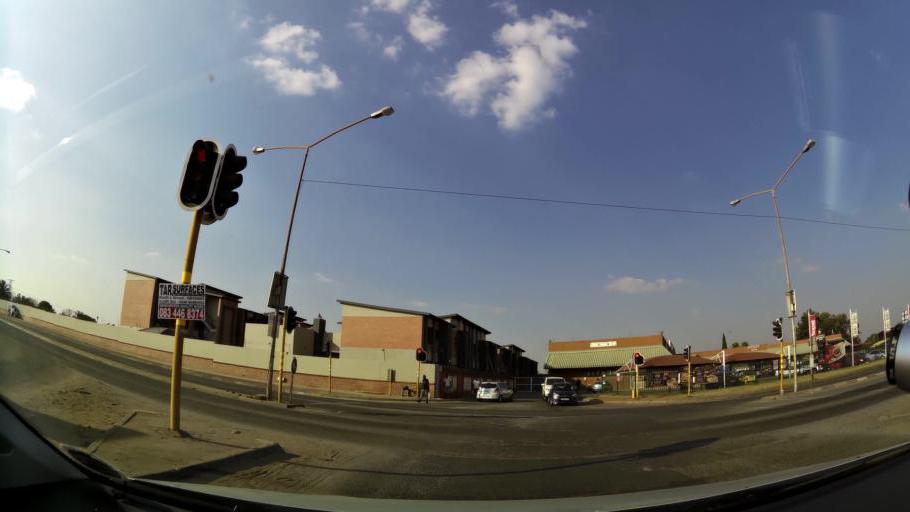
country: ZA
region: Gauteng
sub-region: City of Johannesburg Metropolitan Municipality
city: Modderfontein
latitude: -26.0694
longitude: 28.2075
